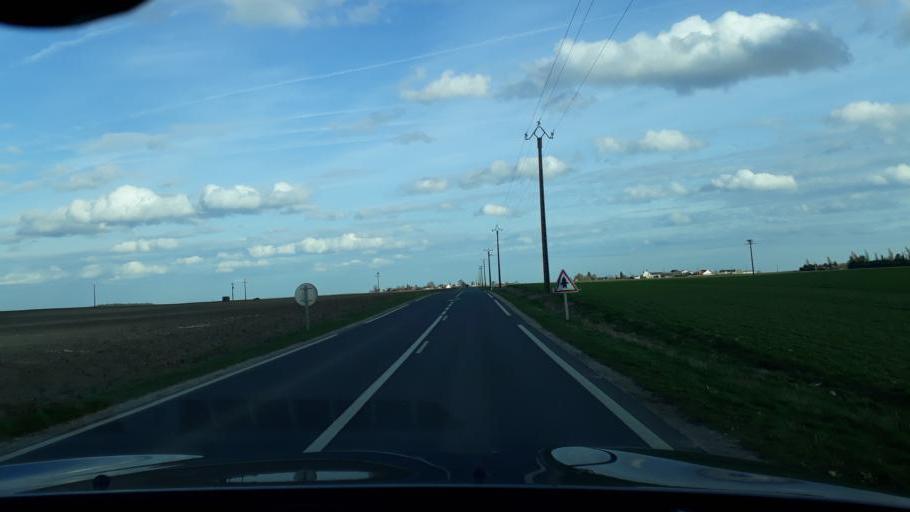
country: FR
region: Centre
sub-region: Departement du Loiret
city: Neuville-aux-Bois
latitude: 48.0699
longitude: 2.0717
